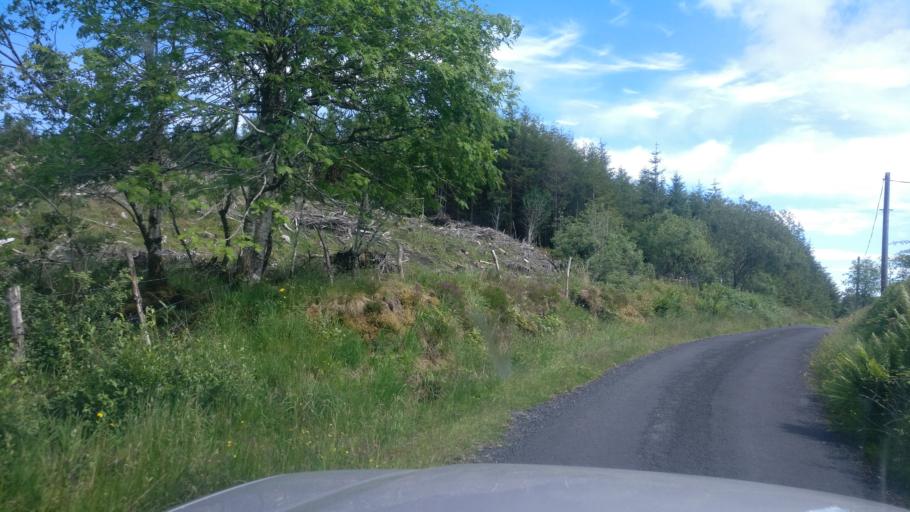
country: IE
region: Connaught
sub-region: County Galway
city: Gort
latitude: 53.0661
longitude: -8.6999
